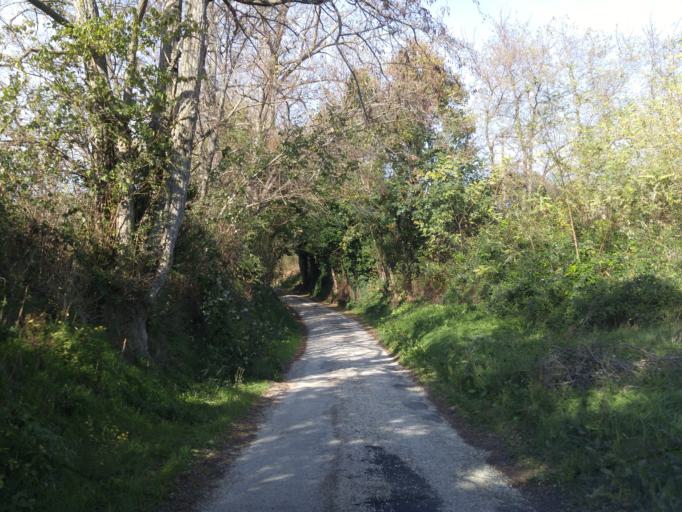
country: IT
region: The Marches
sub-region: Provincia di Pesaro e Urbino
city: Saltara
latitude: 43.7652
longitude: 12.9044
